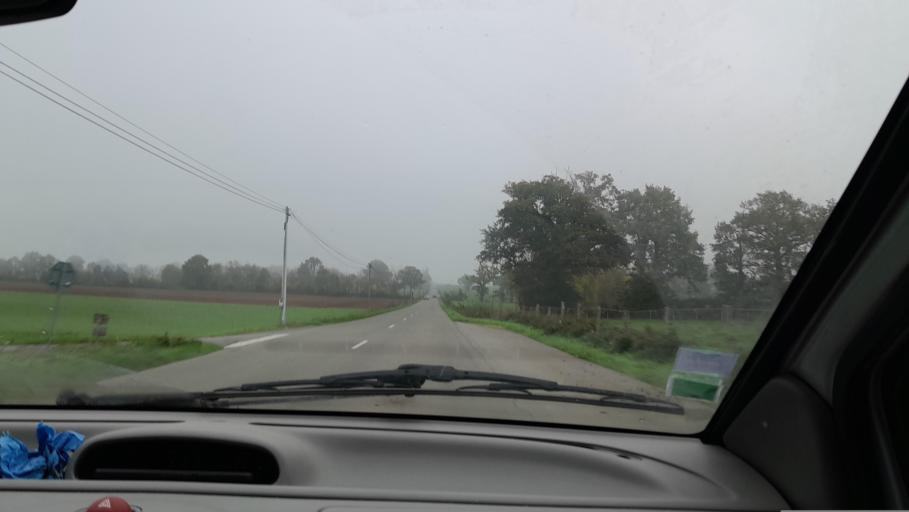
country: FR
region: Brittany
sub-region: Departement d'Ille-et-Vilaine
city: Le Pertre
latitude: 47.9852
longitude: -1.0027
